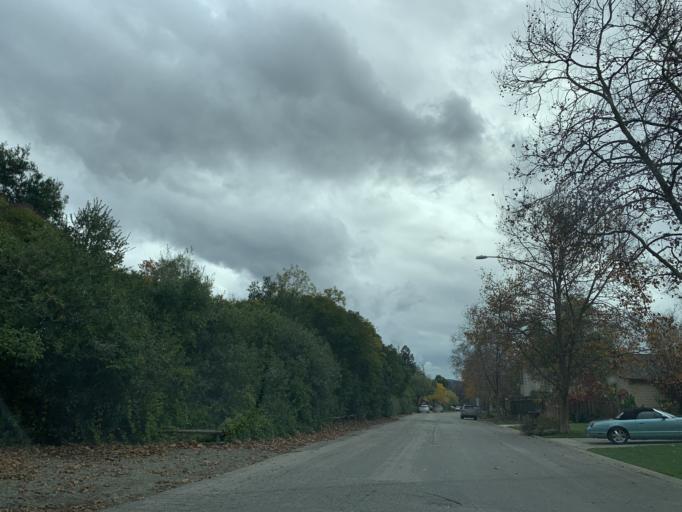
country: US
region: California
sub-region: Santa Clara County
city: Campbell
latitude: 37.2680
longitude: -121.9758
